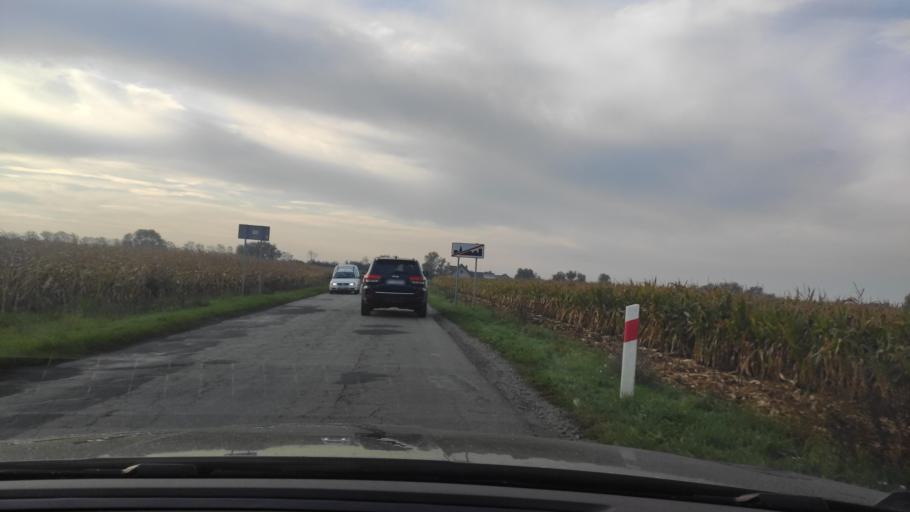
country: PL
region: Greater Poland Voivodeship
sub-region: Powiat poznanski
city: Kleszczewo
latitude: 52.3739
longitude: 17.1665
